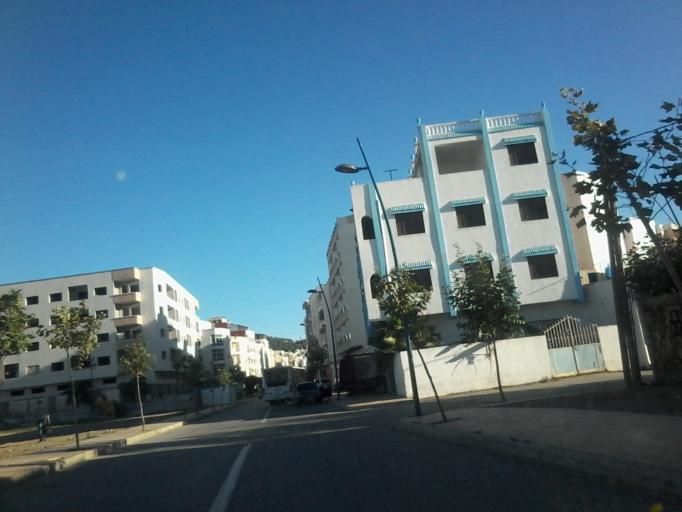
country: MA
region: Tanger-Tetouan
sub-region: Tetouan
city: Martil
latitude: 35.6886
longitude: -5.3279
